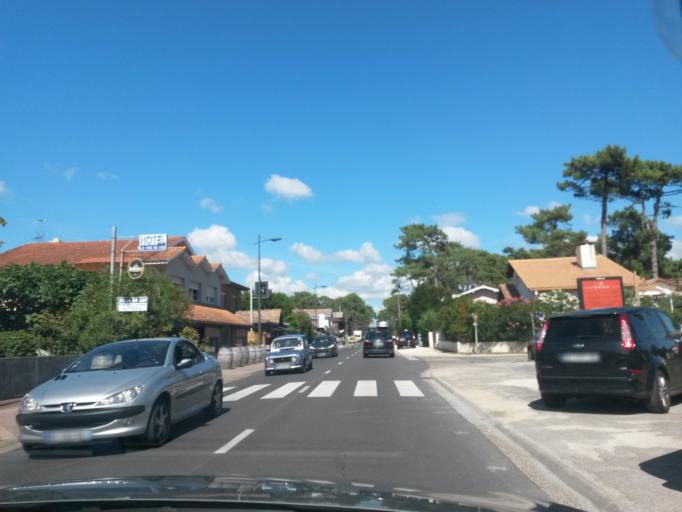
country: FR
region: Aquitaine
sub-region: Departement de la Gironde
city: Arcachon
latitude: 44.7021
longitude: -1.2287
